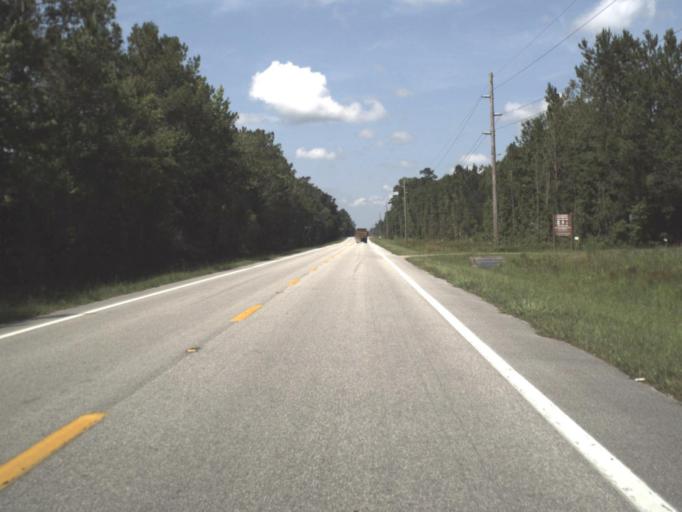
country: US
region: Florida
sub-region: Levy County
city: Bronson
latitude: 29.3581
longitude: -82.7316
